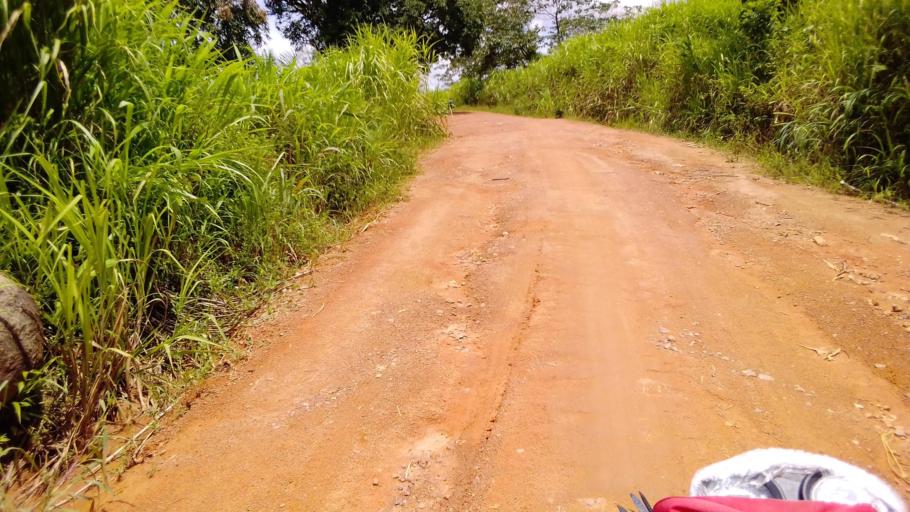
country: SL
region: Eastern Province
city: Koidu
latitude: 8.6703
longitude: -10.9437
